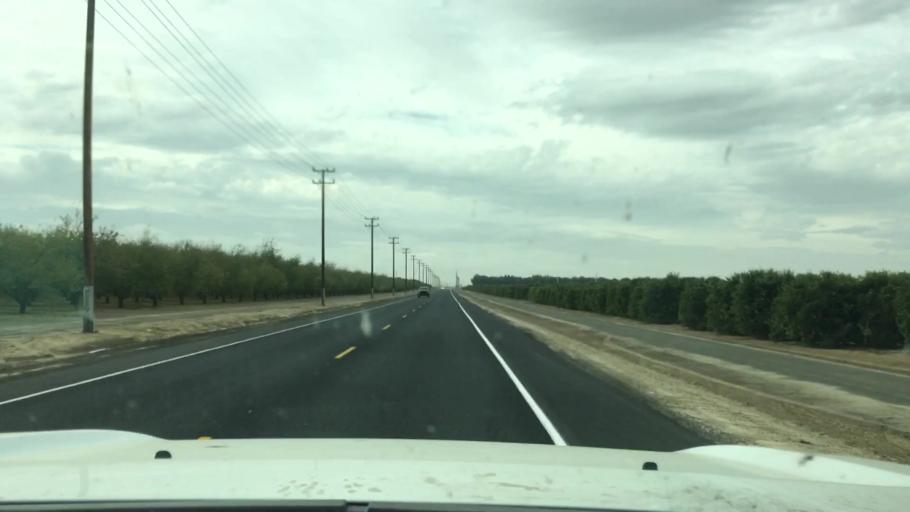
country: US
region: California
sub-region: Kern County
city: Lost Hills
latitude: 35.4992
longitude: -119.7285
